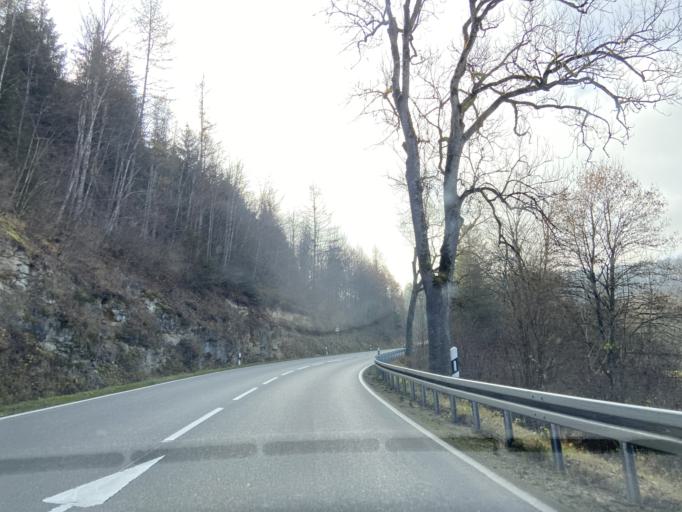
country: DE
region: Baden-Wuerttemberg
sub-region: Tuebingen Region
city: Hettingen
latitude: 48.2300
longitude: 9.2272
